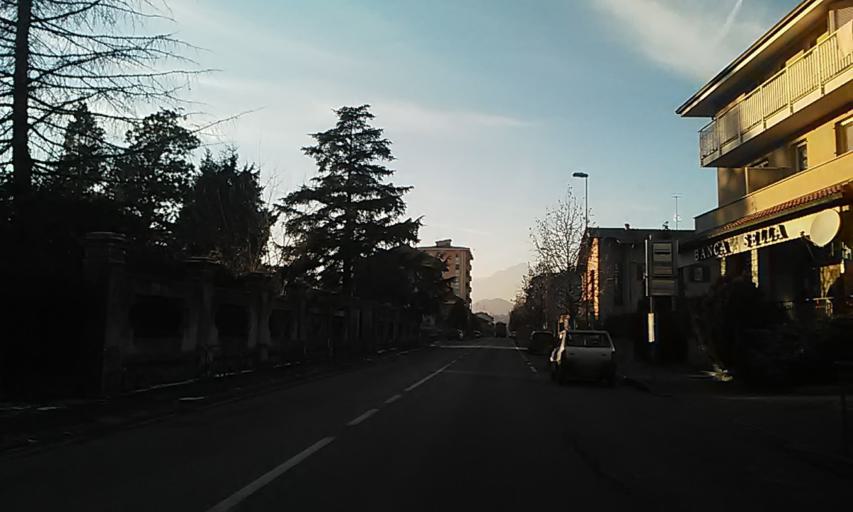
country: IT
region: Piedmont
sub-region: Provincia di Biella
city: Cossato
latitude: 45.5673
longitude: 8.1915
